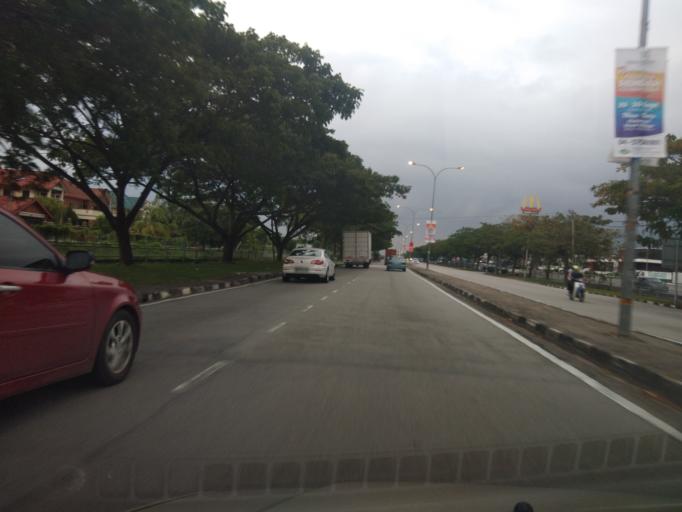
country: MY
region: Penang
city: Kepala Batas
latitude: 5.5181
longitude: 100.4491
